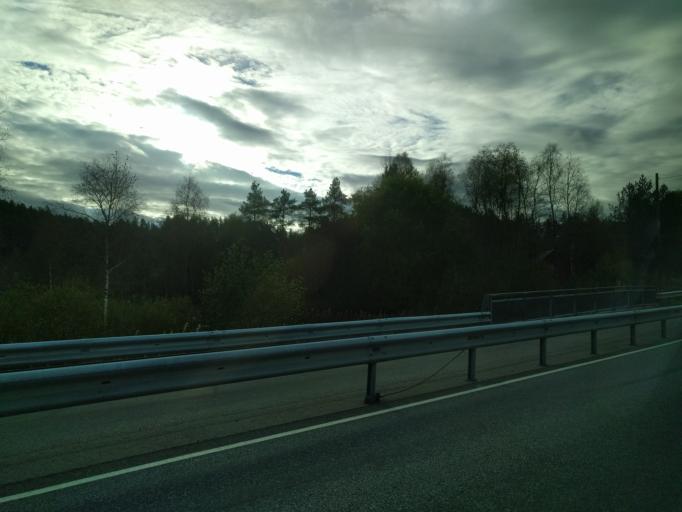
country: NO
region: Vest-Agder
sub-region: Songdalen
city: Nodeland
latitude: 58.2718
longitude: 7.8287
